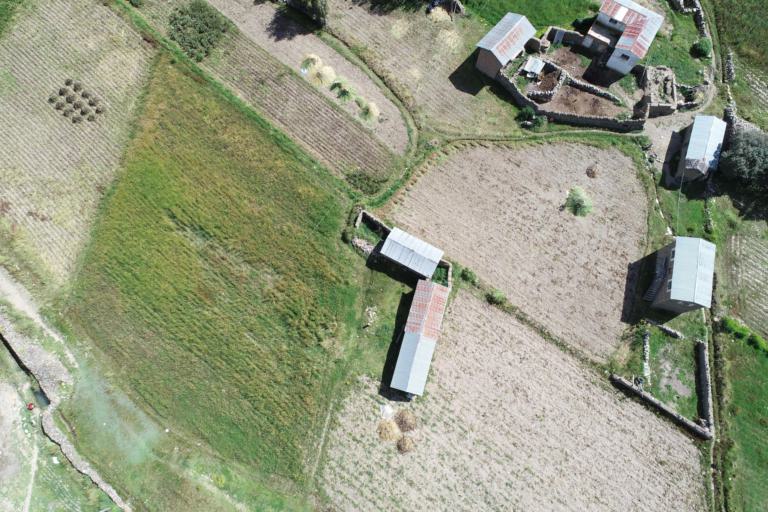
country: BO
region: La Paz
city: Achacachi
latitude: -16.0182
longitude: -68.6161
